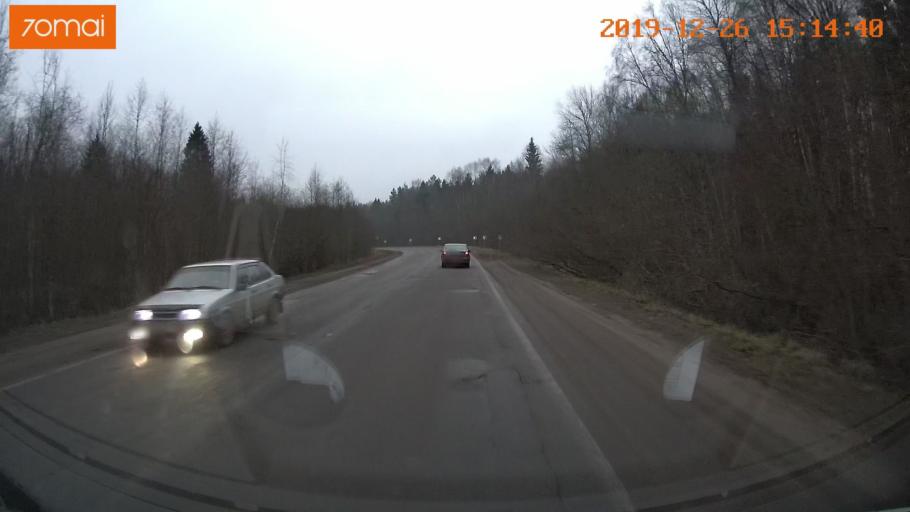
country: RU
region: Jaroslavl
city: Rybinsk
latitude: 58.1042
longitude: 38.8781
